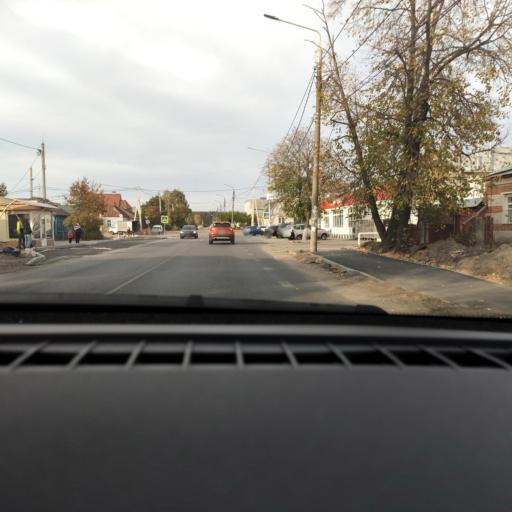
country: RU
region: Voronezj
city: Somovo
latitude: 51.7387
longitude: 39.2672
